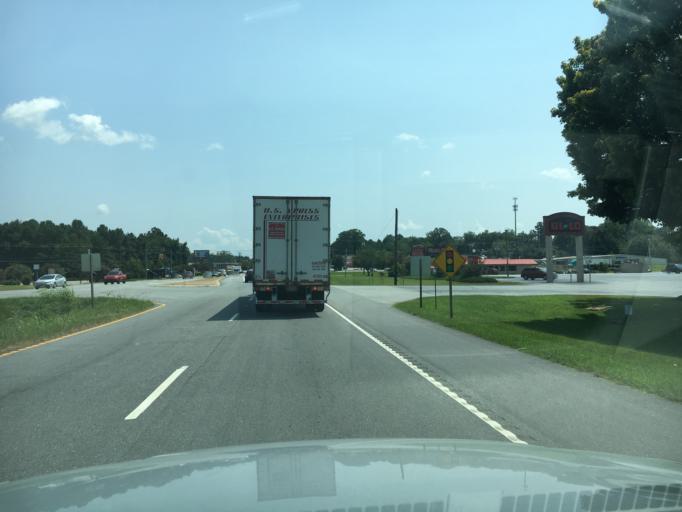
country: US
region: South Carolina
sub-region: Anderson County
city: Pendleton
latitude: 34.6356
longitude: -82.7851
